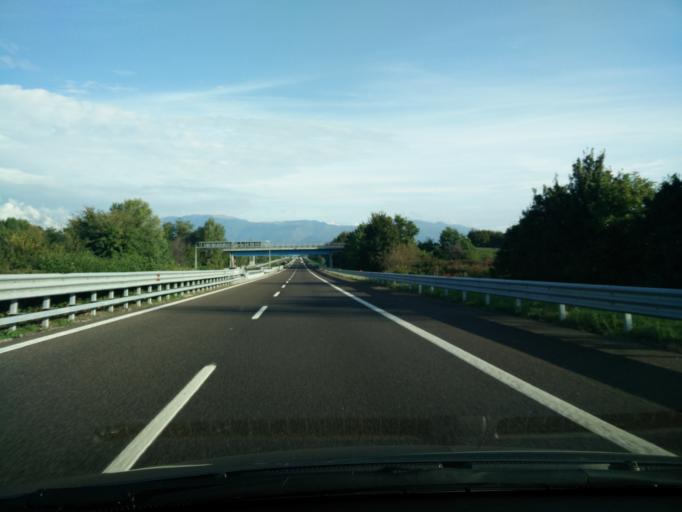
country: IT
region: Veneto
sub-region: Provincia di Treviso
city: San Vendemiano
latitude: 45.8907
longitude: 12.3417
